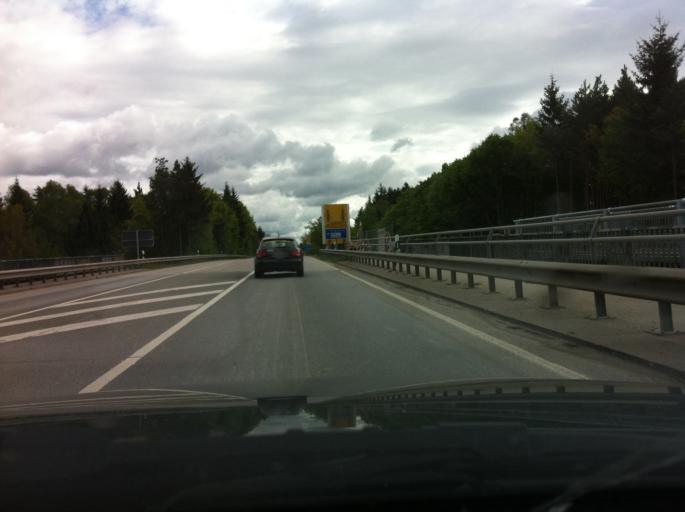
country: DE
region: Bavaria
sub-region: Upper Bavaria
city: Brunnthal
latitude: 47.9777
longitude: 11.6845
